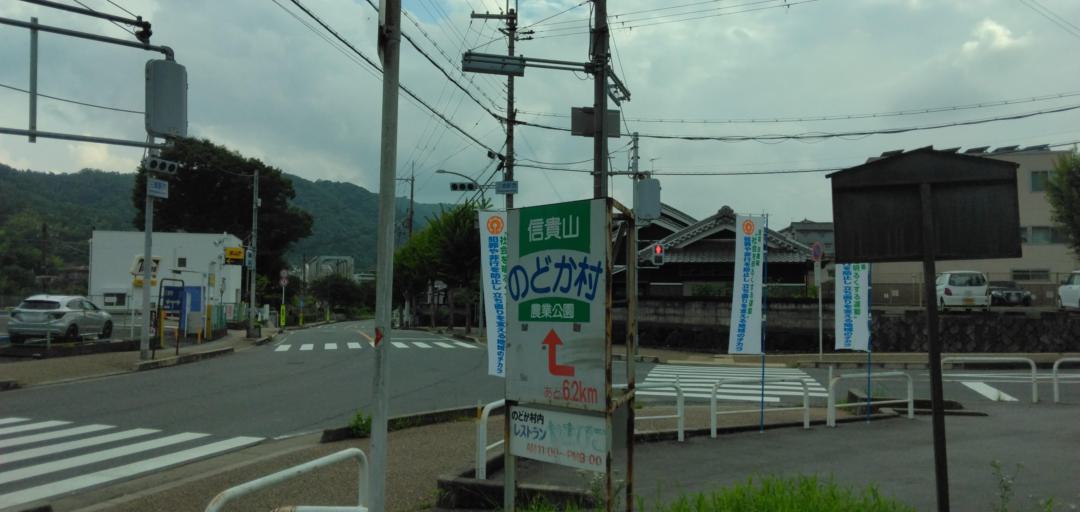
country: JP
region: Osaka
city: Kashihara
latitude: 34.5891
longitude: 135.6865
